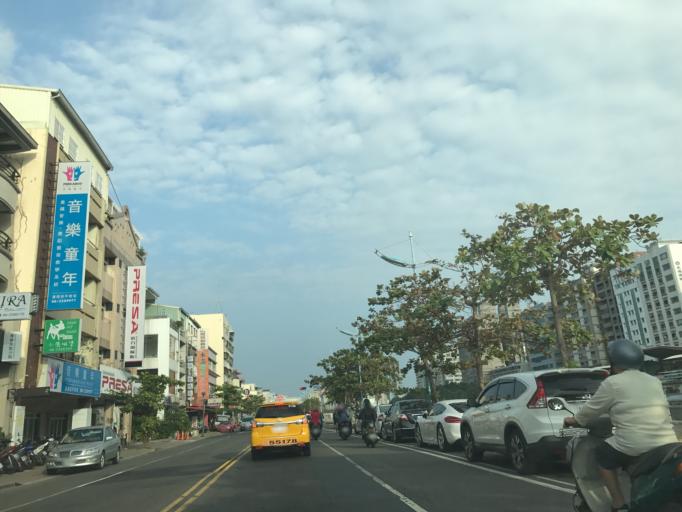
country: TW
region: Taiwan
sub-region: Tainan
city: Tainan
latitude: 22.9983
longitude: 120.1768
